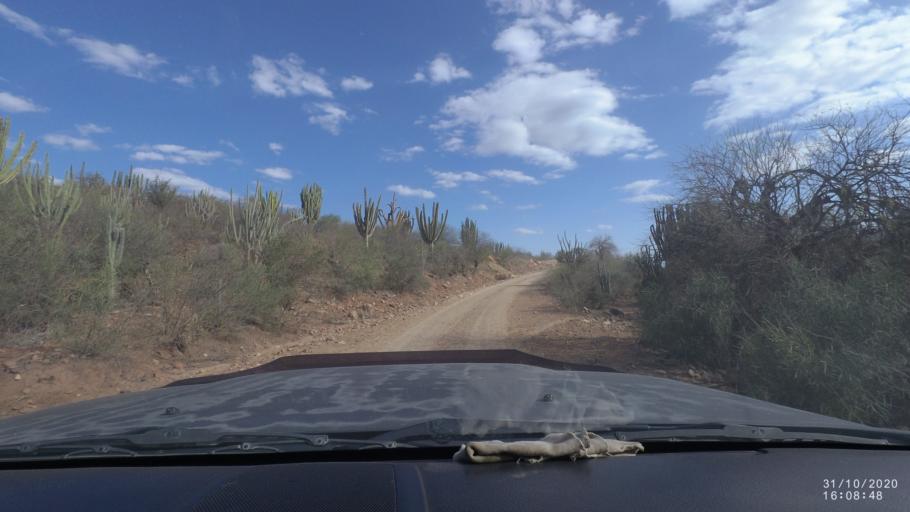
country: BO
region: Chuquisaca
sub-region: Provincia Zudanez
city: Mojocoya
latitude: -18.3852
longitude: -64.6389
